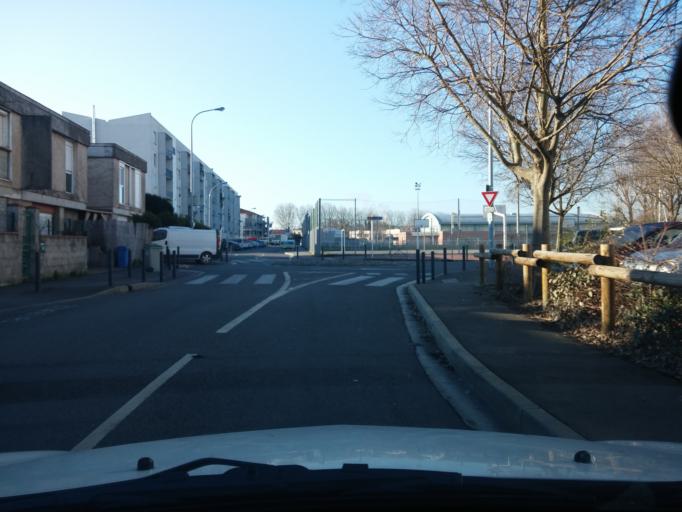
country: FR
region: Midi-Pyrenees
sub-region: Departement de la Haute-Garonne
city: Toulouse
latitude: 43.5791
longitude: 1.4171
